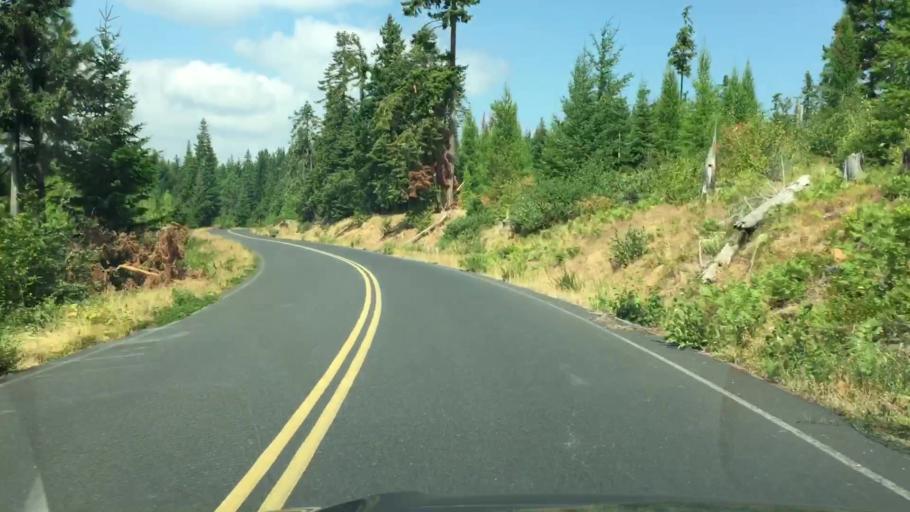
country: US
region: Washington
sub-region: Klickitat County
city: White Salmon
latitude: 46.0323
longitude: -121.5433
